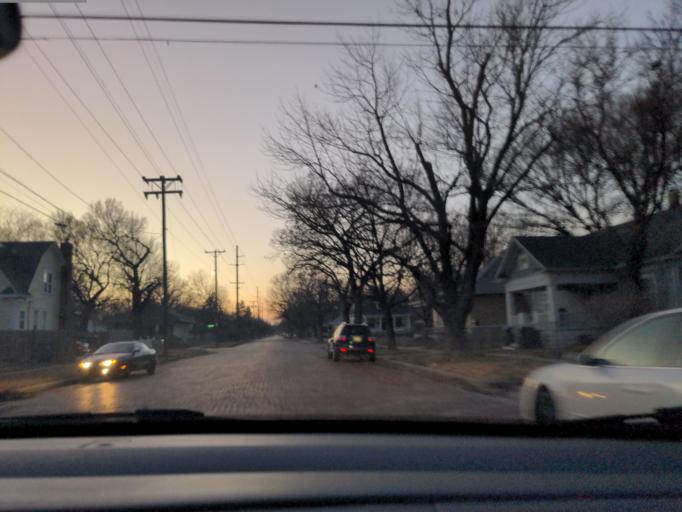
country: US
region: Kansas
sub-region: Sedgwick County
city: Wichita
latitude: 37.7044
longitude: -97.3425
